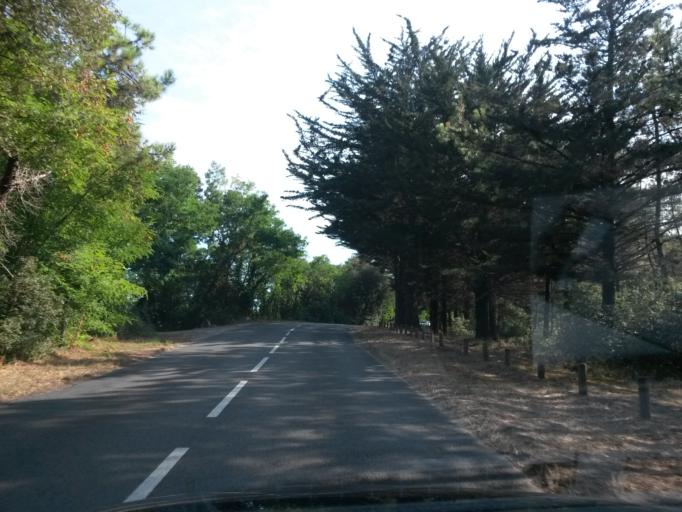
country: FR
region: Pays de la Loire
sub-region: Departement de la Vendee
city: Olonne-sur-Mer
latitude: 46.5396
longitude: -1.8124
